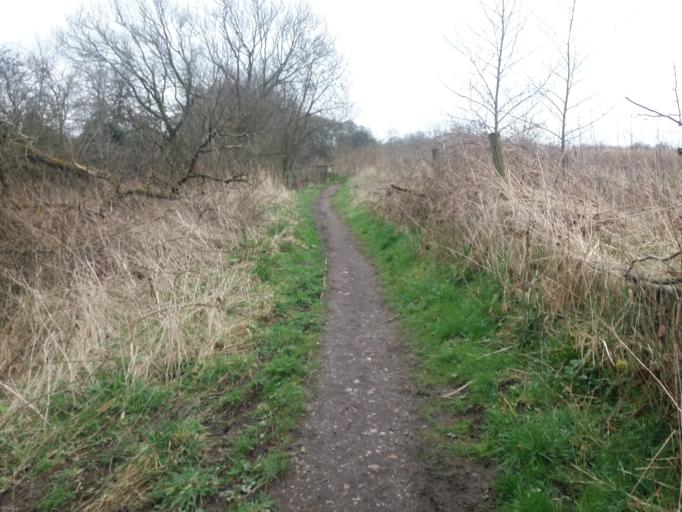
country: GB
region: England
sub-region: Lancashire
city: Chorley
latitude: 53.6569
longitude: -2.6124
